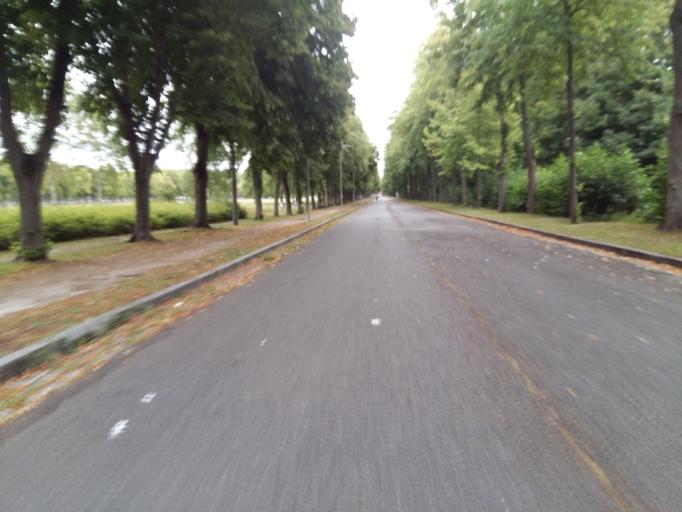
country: FR
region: Picardie
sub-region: Departement de la Somme
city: Amiens
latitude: 49.8982
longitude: 2.2752
